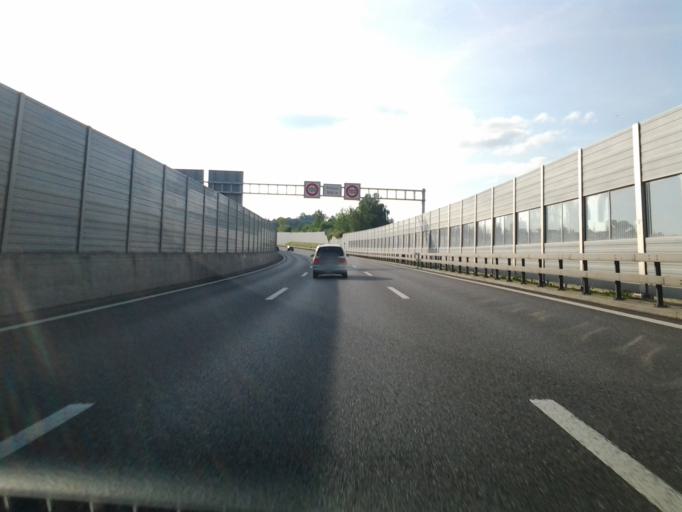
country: CH
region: Lucerne
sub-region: Hochdorf District
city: Emmen
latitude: 47.0799
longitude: 8.2894
